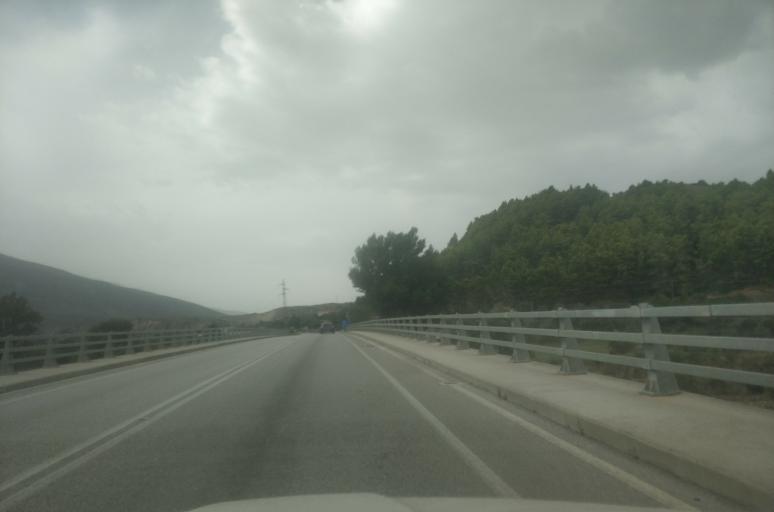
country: AL
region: Gjirokaster
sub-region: Rrethi i Tepelenes
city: Memaliaj
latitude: 40.3523
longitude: 19.9557
